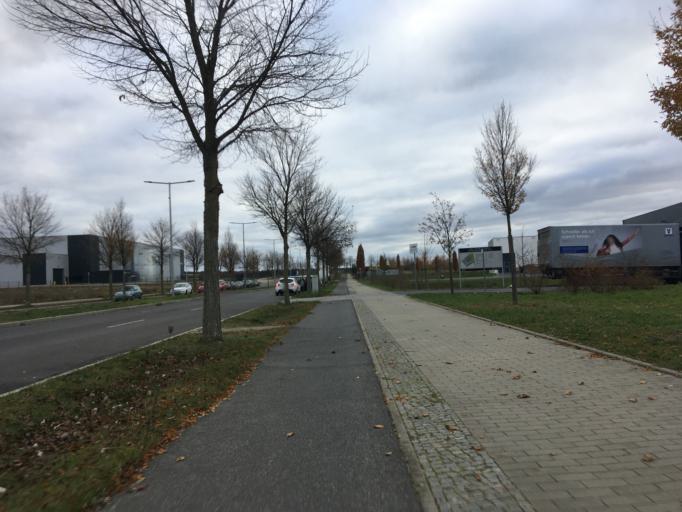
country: DE
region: Berlin
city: Altglienicke
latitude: 52.3937
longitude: 13.5442
